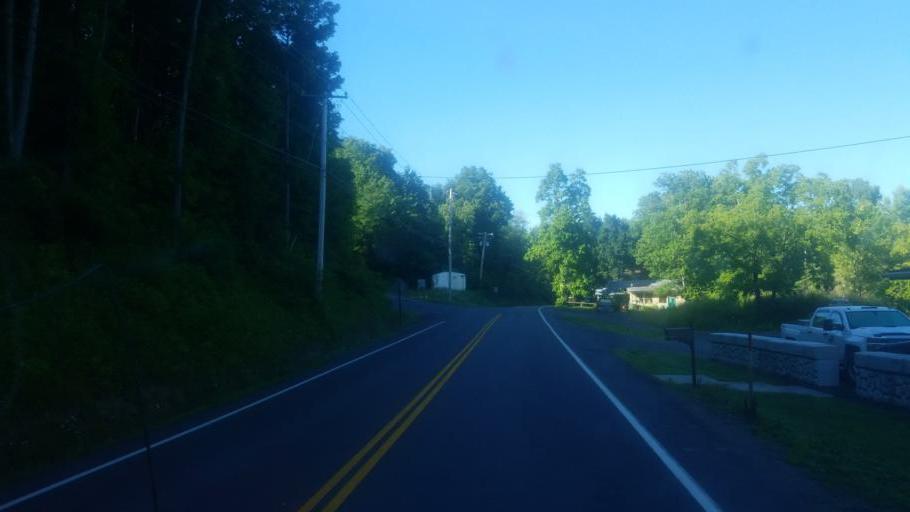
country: US
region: New York
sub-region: Wayne County
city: Newark
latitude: 43.0747
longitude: -77.0760
